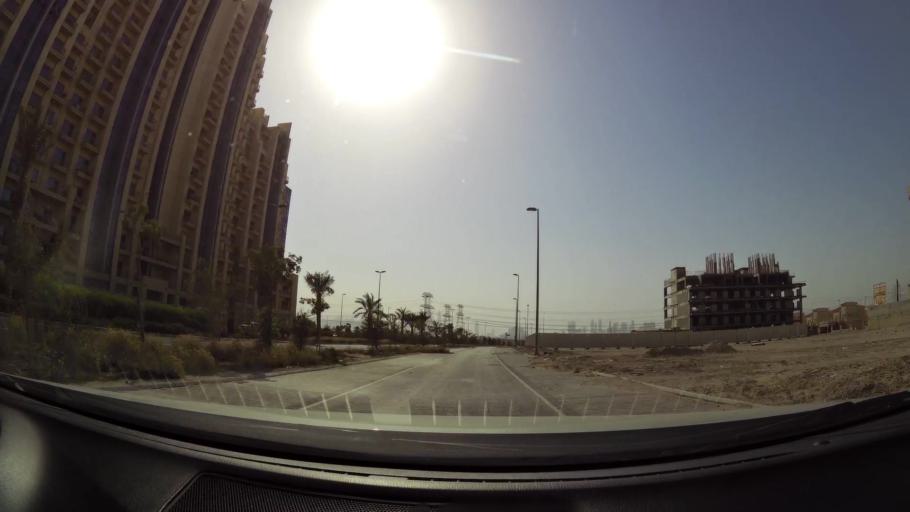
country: AE
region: Dubai
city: Dubai
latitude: 25.0691
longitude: 55.2081
